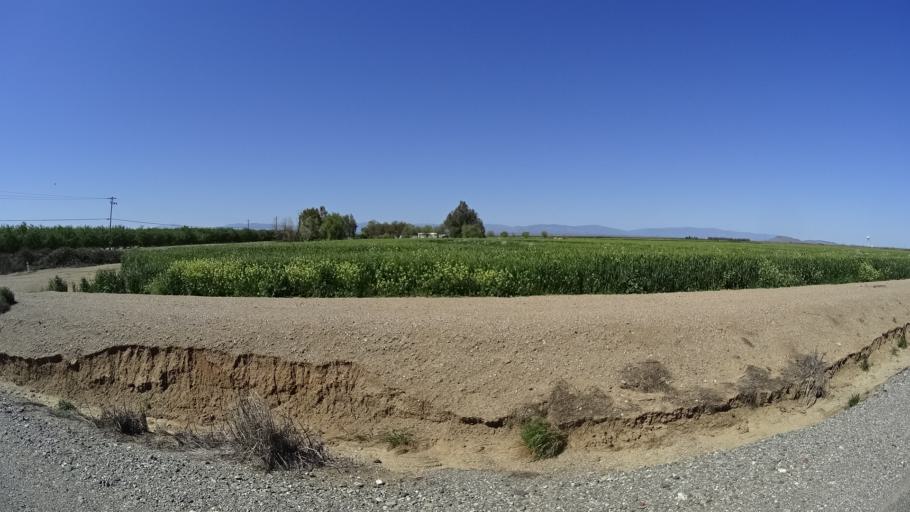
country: US
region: California
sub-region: Glenn County
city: Orland
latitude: 39.6688
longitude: -122.2342
